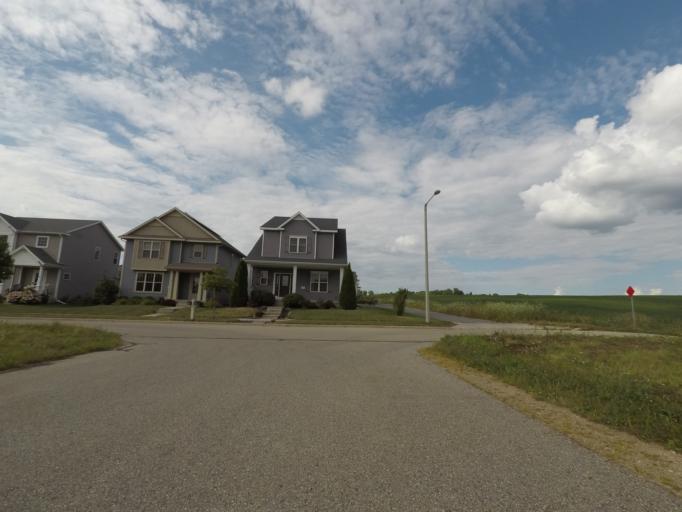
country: US
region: Wisconsin
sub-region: Dane County
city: Middleton
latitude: 43.0552
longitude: -89.5474
